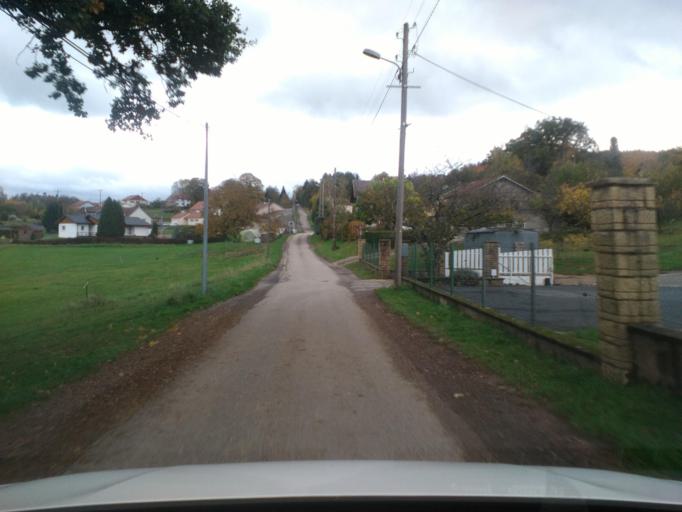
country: FR
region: Lorraine
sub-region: Departement des Vosges
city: Moyenmoutier
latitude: 48.3705
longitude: 6.8902
